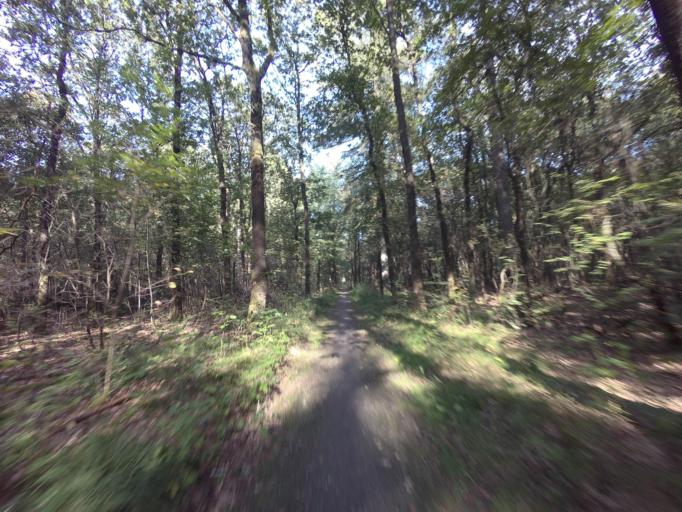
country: NL
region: Drenthe
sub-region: Gemeente Tynaarlo
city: Vries
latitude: 53.0760
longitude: 6.5142
